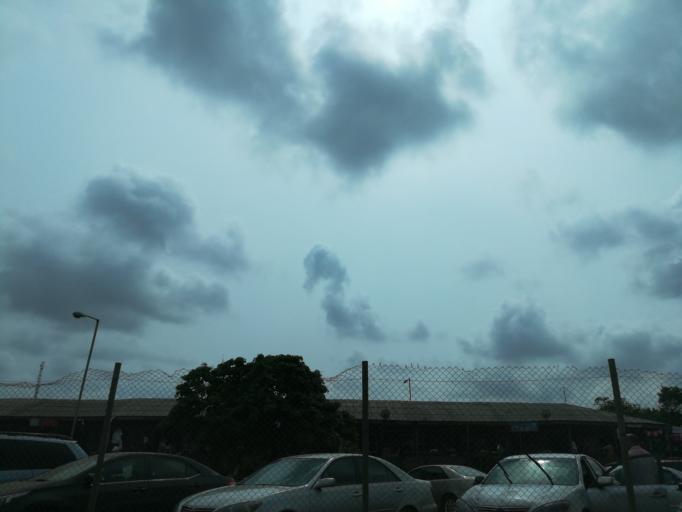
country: NG
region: Lagos
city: Oshodi
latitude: 6.5751
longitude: 3.3234
